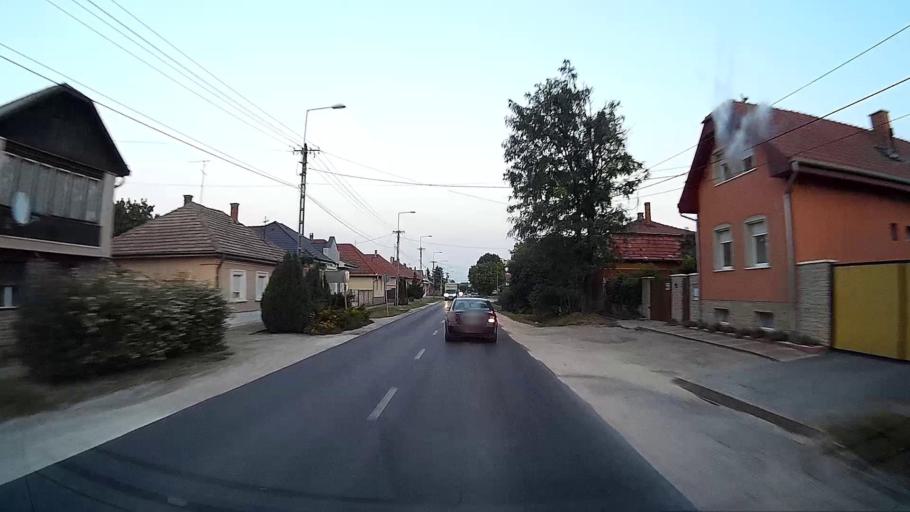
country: HU
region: Pest
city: Albertirsa
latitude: 47.2495
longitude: 19.6091
